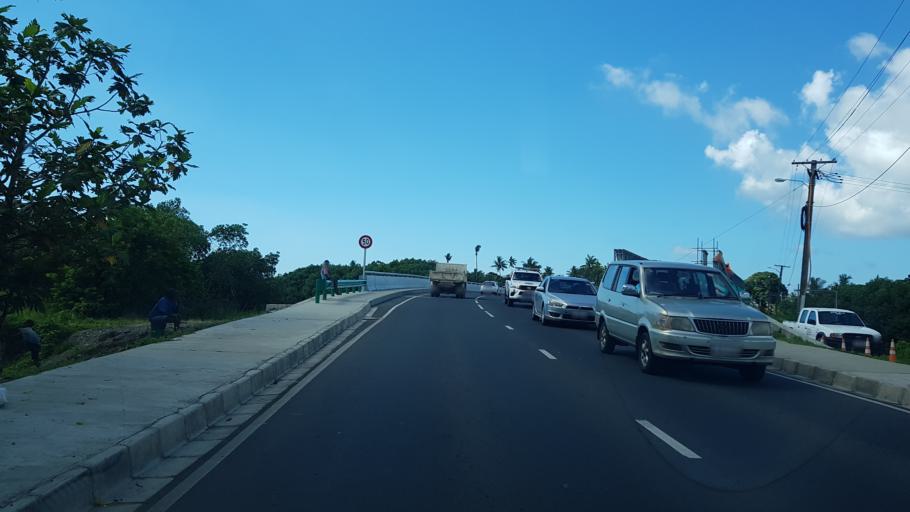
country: FJ
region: Central
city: Suva
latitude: -18.1378
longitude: 178.4585
